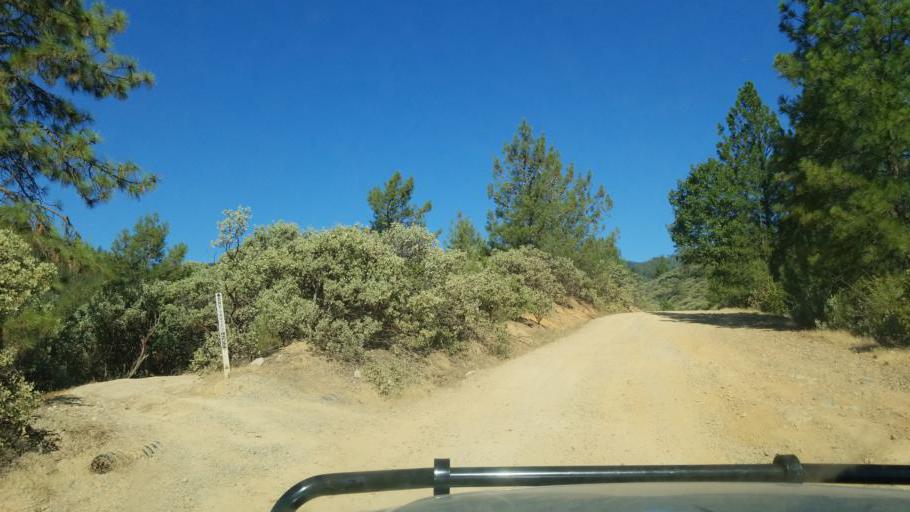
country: US
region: California
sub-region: Shasta County
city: Shasta
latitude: 40.6593
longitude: -122.4656
